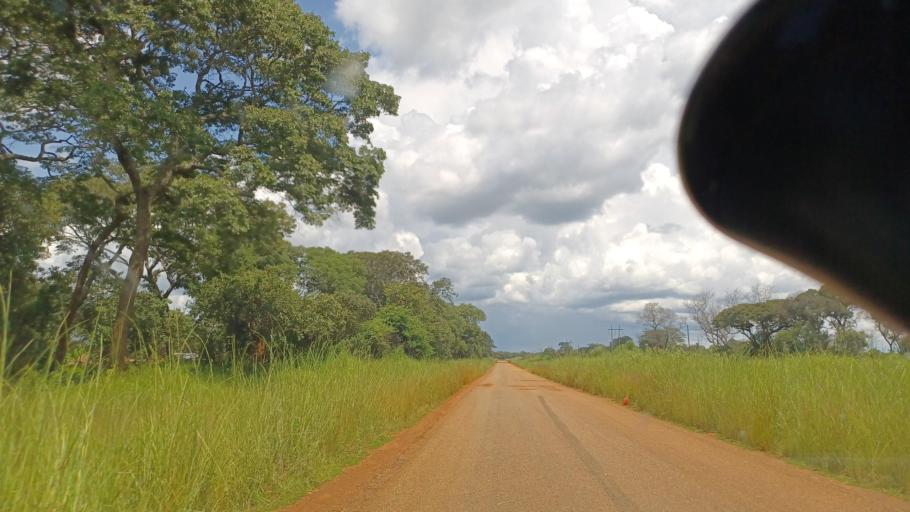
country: ZM
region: North-Western
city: Solwezi
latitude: -12.6857
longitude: 26.0406
